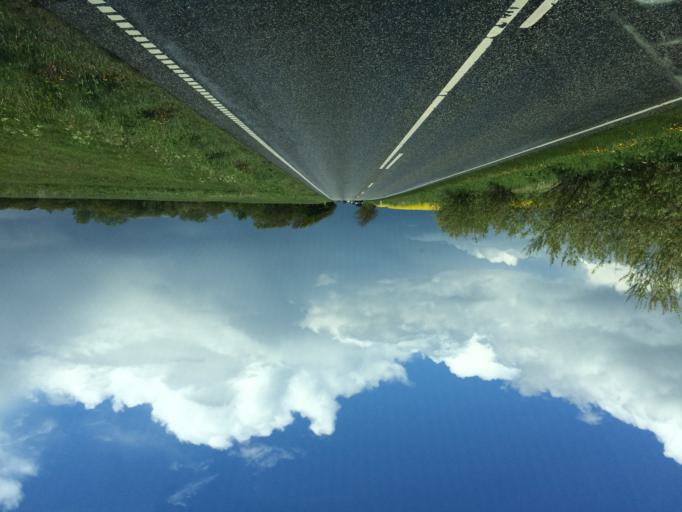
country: DK
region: Central Jutland
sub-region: Holstebro Kommune
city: Vinderup
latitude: 56.4267
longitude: 8.7097
